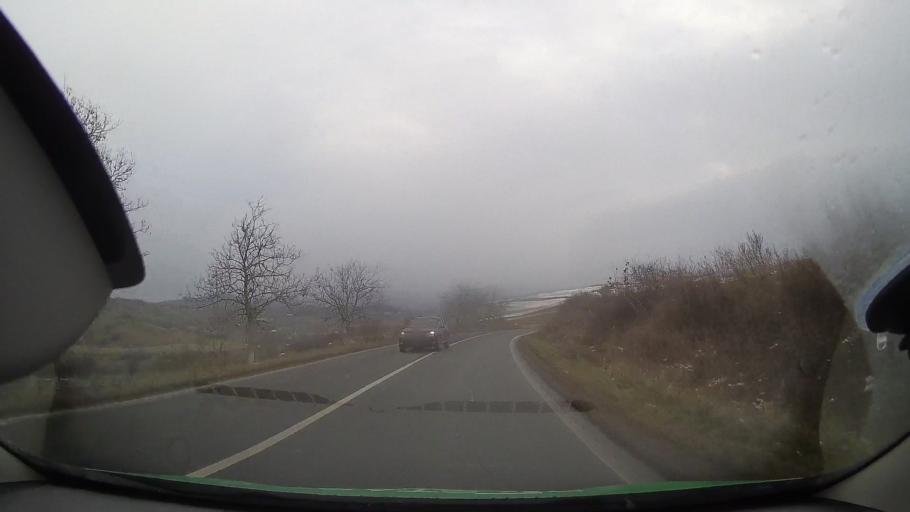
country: RO
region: Sibiu
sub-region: Comuna Blajel
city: Blajel
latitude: 46.2428
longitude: 24.3020
